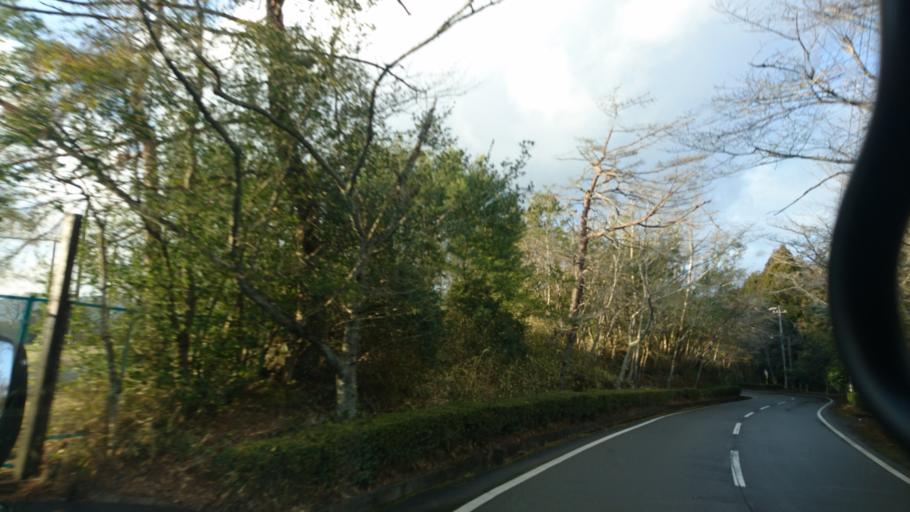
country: JP
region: Mie
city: Ueno-ebisumachi
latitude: 34.7529
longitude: 136.0523
